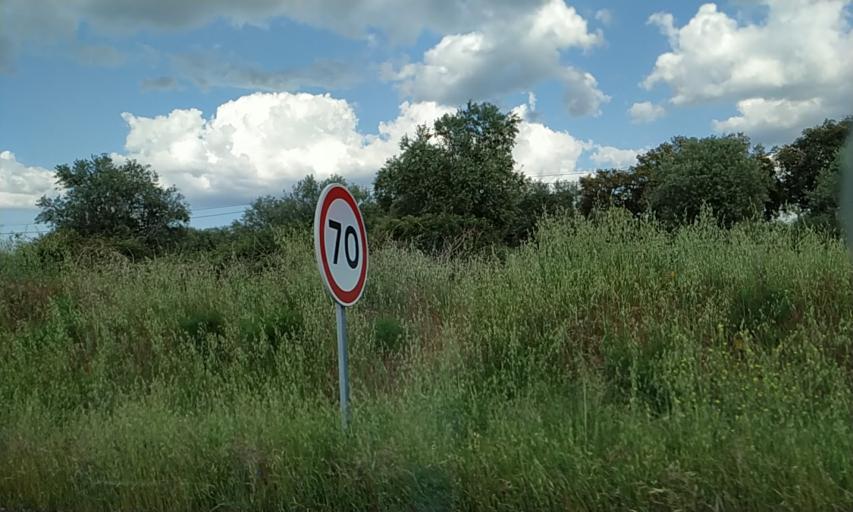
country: PT
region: Portalegre
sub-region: Portalegre
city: Portalegre
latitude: 39.2551
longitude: -7.4471
